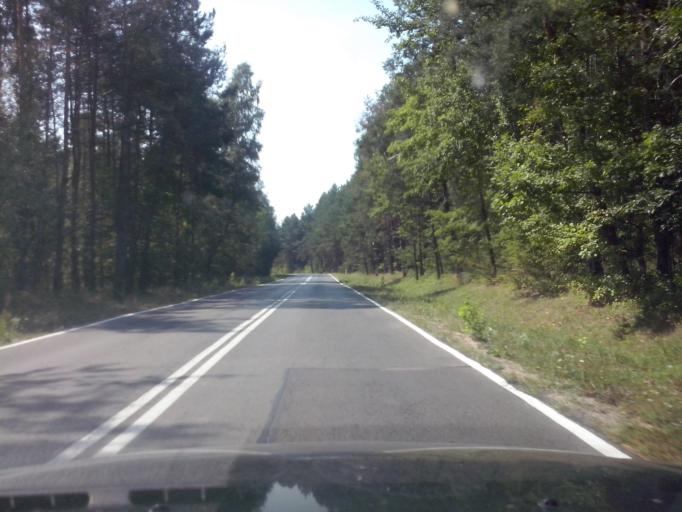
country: PL
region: Swietokrzyskie
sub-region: Powiat staszowski
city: Szydlow
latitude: 50.6224
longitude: 21.0175
